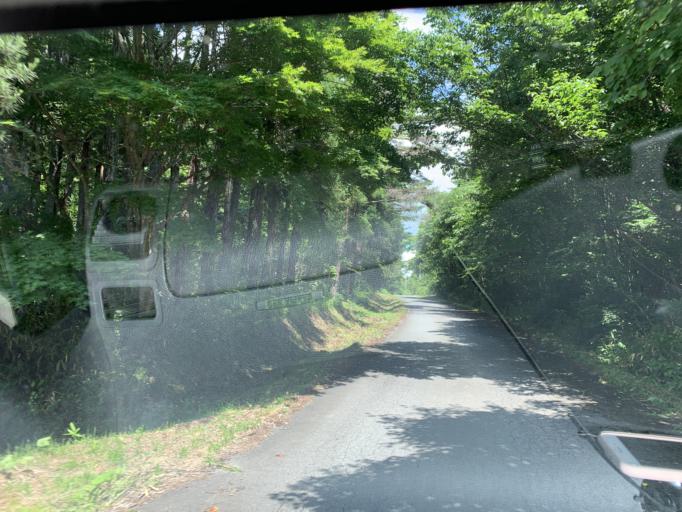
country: JP
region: Iwate
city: Ichinoseki
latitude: 38.9246
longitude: 141.0498
